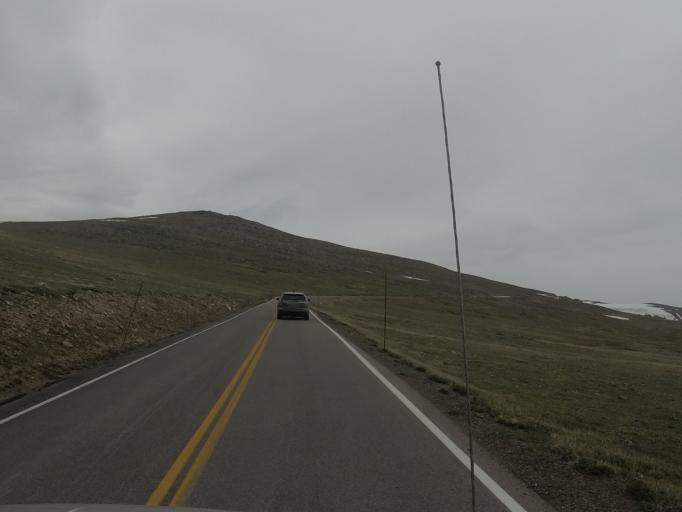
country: US
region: Montana
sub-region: Carbon County
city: Red Lodge
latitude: 44.9982
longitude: -109.4209
